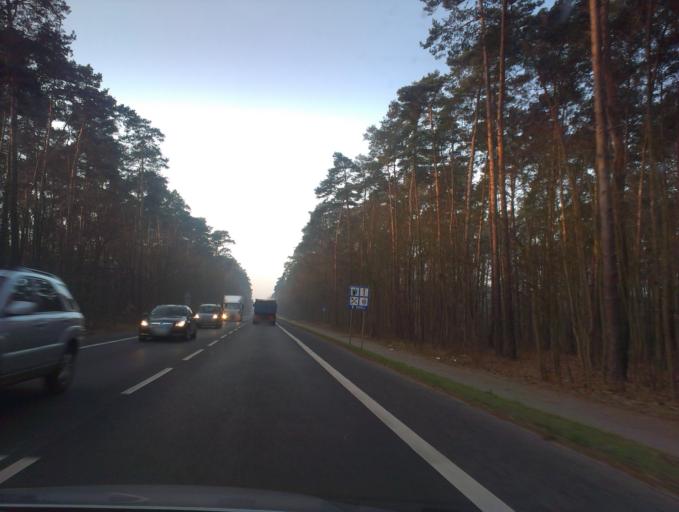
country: PL
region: Greater Poland Voivodeship
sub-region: Powiat obornicki
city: Oborniki
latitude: 52.6768
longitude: 16.8649
